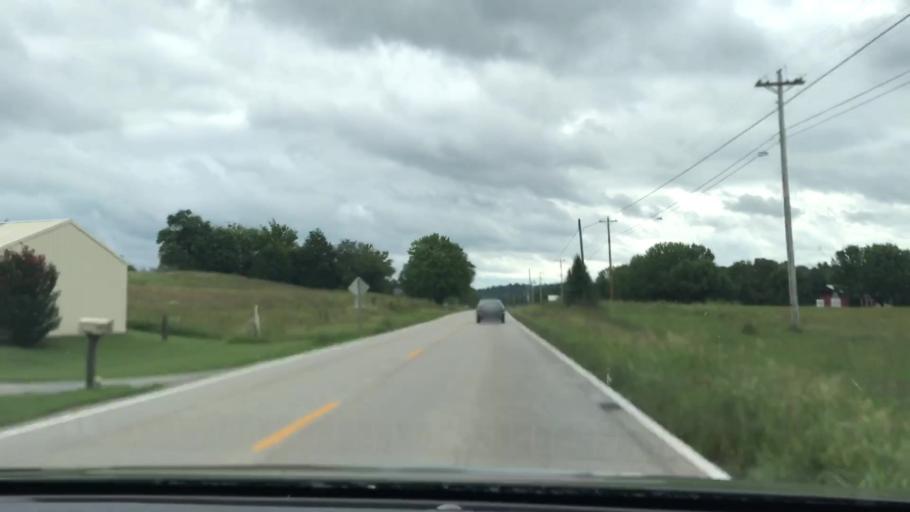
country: US
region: Kentucky
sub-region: Metcalfe County
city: Edmonton
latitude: 36.9028
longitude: -85.7517
